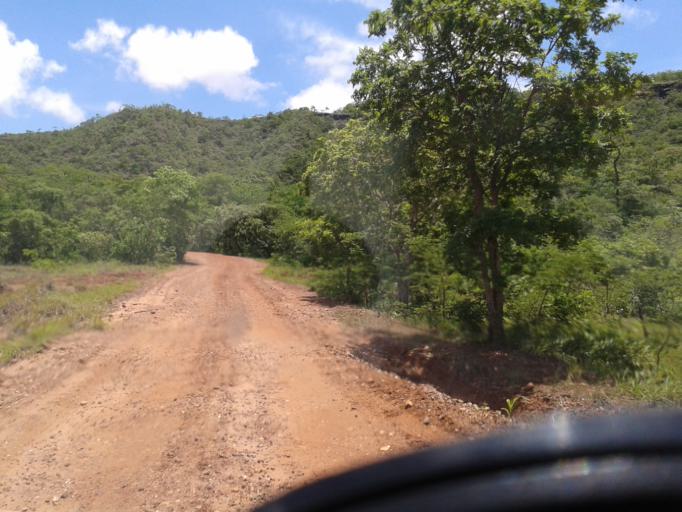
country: BR
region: Minas Gerais
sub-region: Santa Vitoria
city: Santa Vitoria
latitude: -18.9853
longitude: -49.8973
